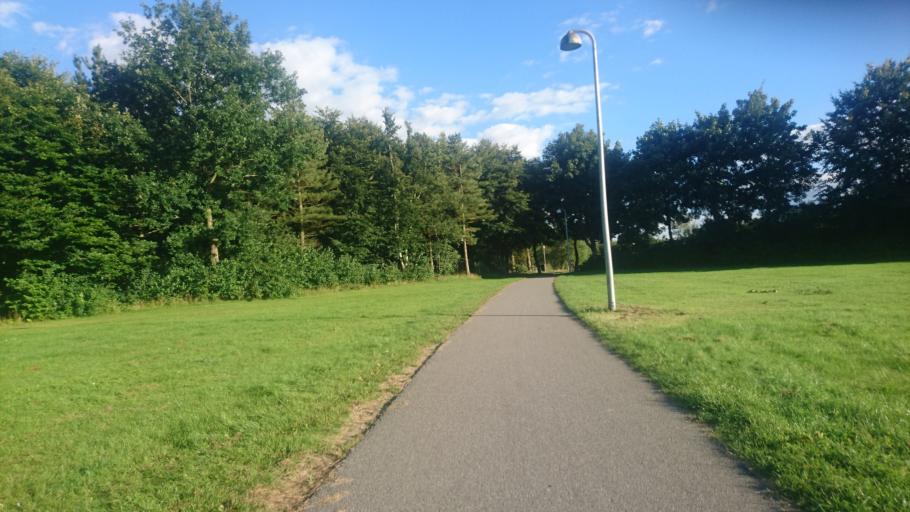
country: DK
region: South Denmark
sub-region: Billund Kommune
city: Billund
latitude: 55.7237
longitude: 9.1066
